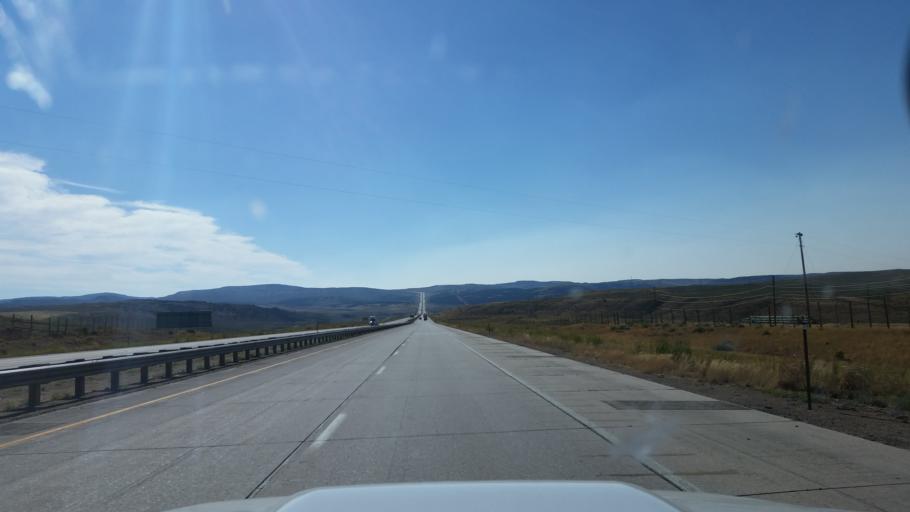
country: US
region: Wyoming
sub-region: Uinta County
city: Mountain View
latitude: 41.2981
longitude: -110.5972
